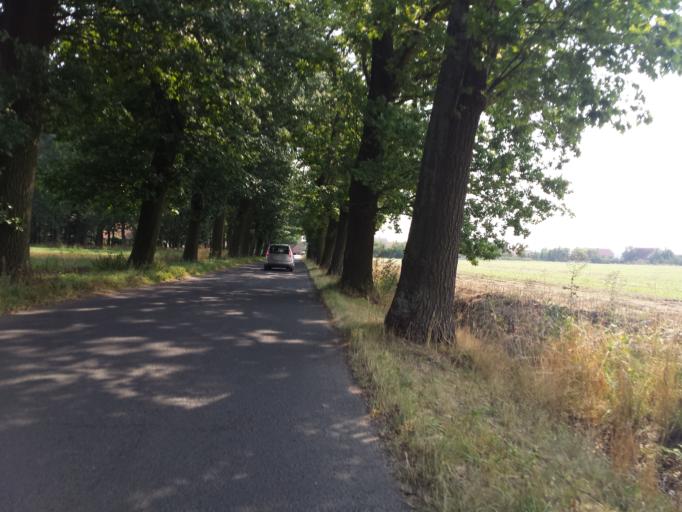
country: PL
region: Greater Poland Voivodeship
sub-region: Powiat czarnkowsko-trzcianecki
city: Polajewo
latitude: 52.7744
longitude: 16.6323
